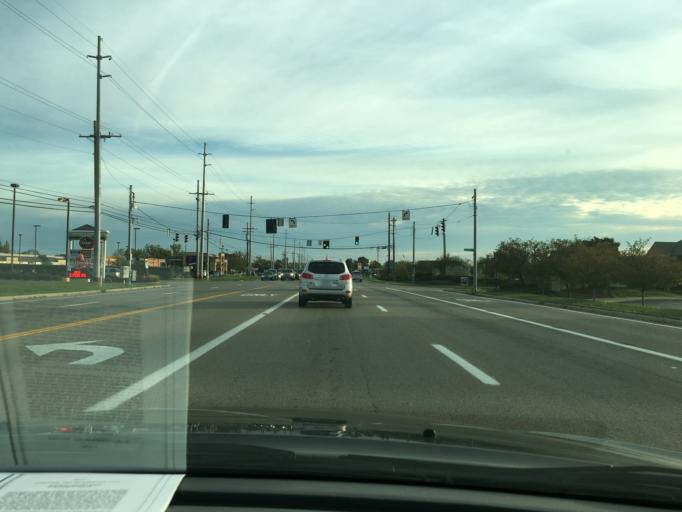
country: US
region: Ohio
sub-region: Butler County
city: Beckett Ridge
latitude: 39.3554
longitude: -84.4612
